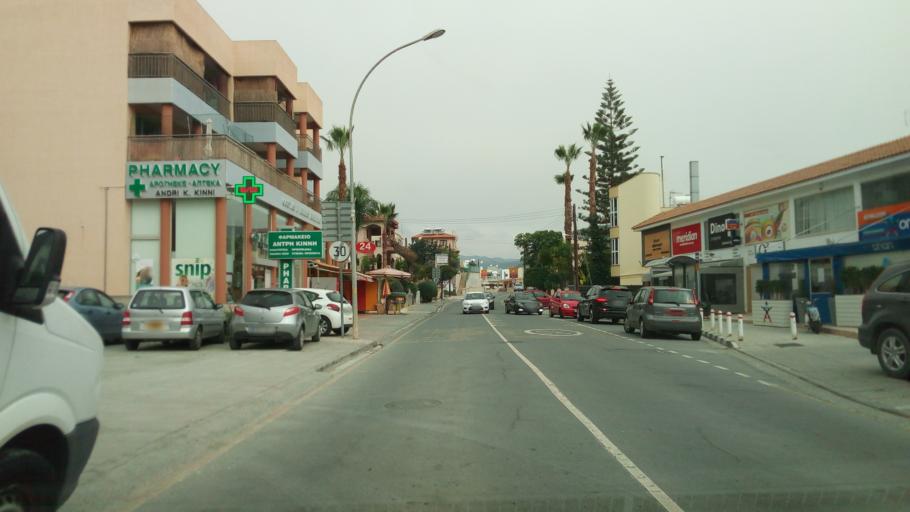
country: CY
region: Limassol
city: Mouttagiaka
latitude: 34.7153
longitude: 33.0861
